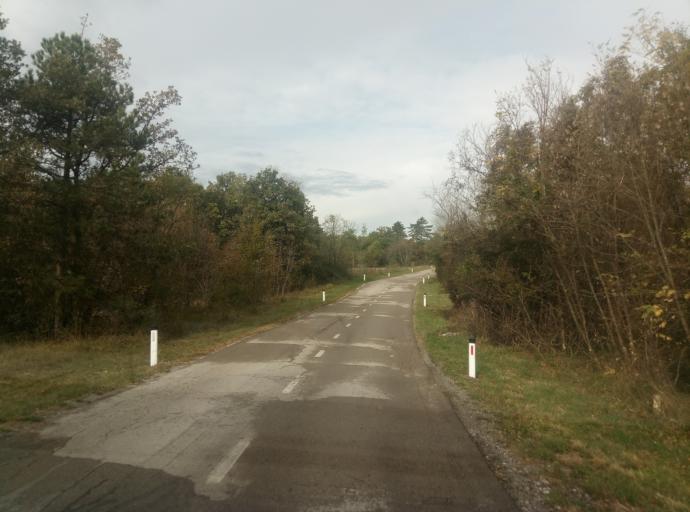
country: SI
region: Sezana
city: Sezana
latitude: 45.7743
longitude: 13.8731
